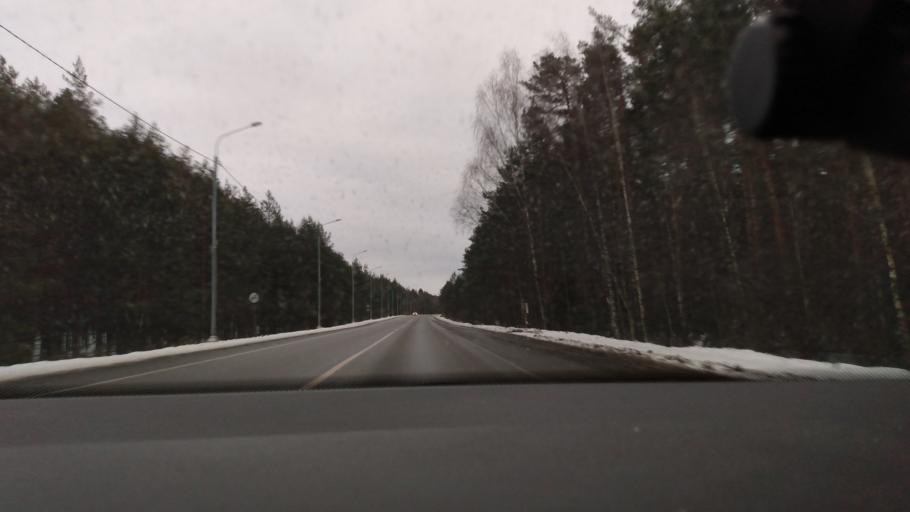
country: RU
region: Moskovskaya
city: Il'inskiy Pogost
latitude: 55.4769
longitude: 38.9463
